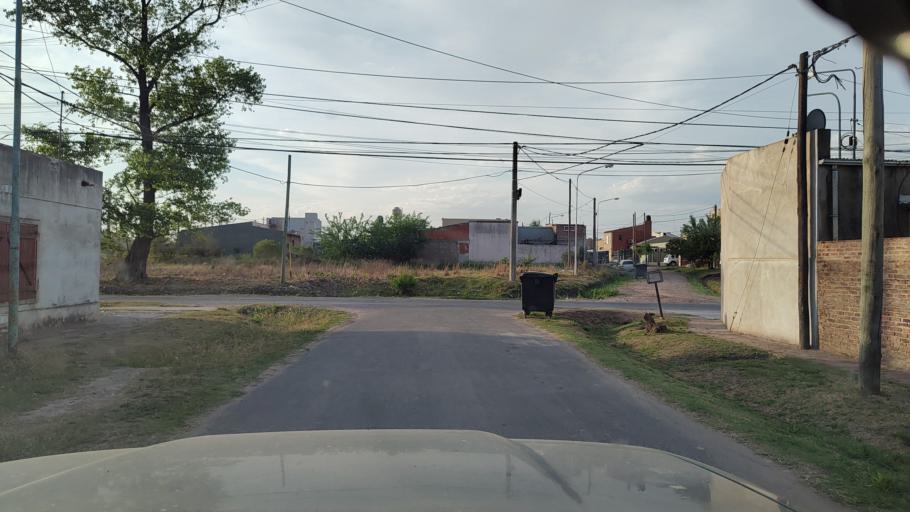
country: AR
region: Buenos Aires
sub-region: Partido de Lujan
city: Lujan
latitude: -34.5677
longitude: -59.1366
